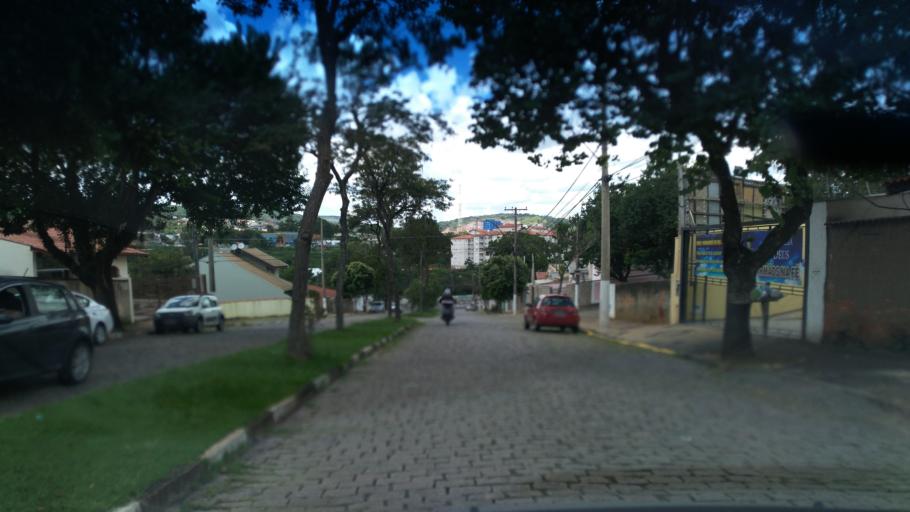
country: BR
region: Sao Paulo
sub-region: Valinhos
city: Valinhos
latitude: -22.9781
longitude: -46.9915
